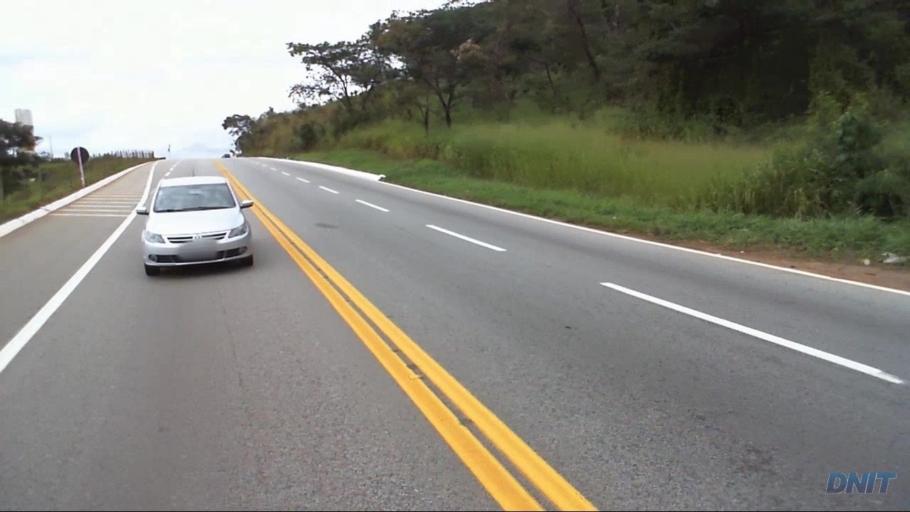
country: BR
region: Minas Gerais
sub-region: Caete
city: Caete
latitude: -19.7885
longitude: -43.6957
